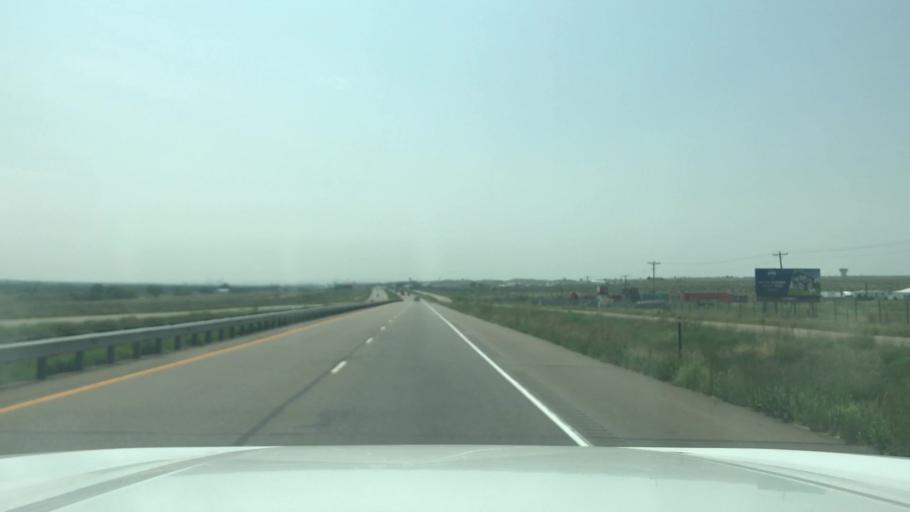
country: US
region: Colorado
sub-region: Pueblo County
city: Pueblo West
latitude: 38.3659
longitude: -104.6209
